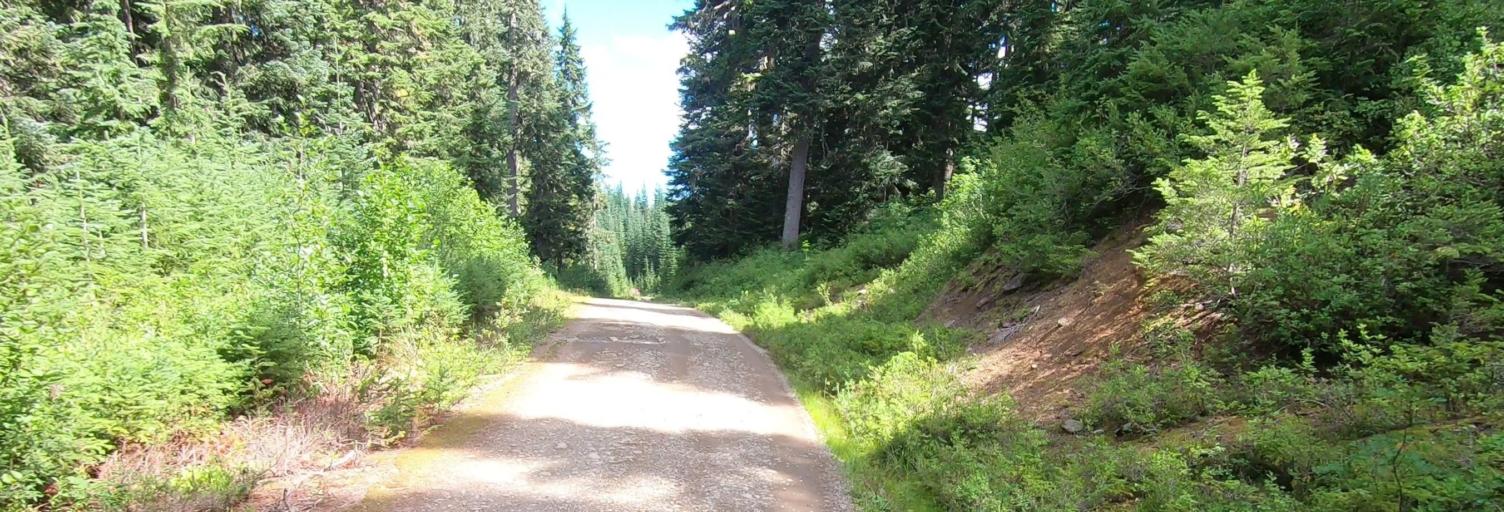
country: CA
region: British Columbia
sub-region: Fraser Valley Regional District
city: Chilliwack
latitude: 48.8698
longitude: -121.7968
